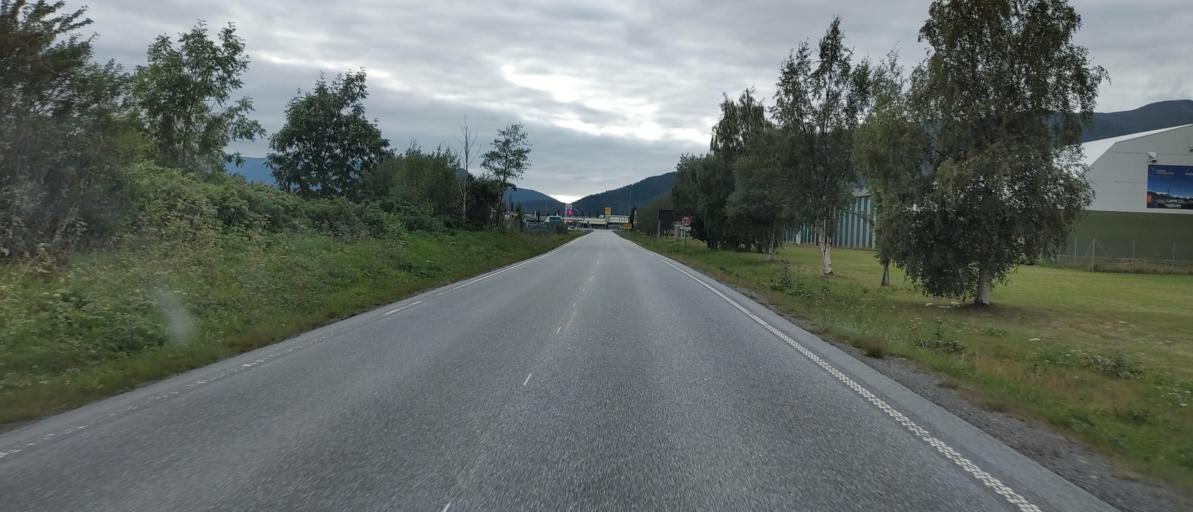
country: NO
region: More og Romsdal
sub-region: Rauma
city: Andalsnes
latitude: 62.5575
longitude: 7.6914
